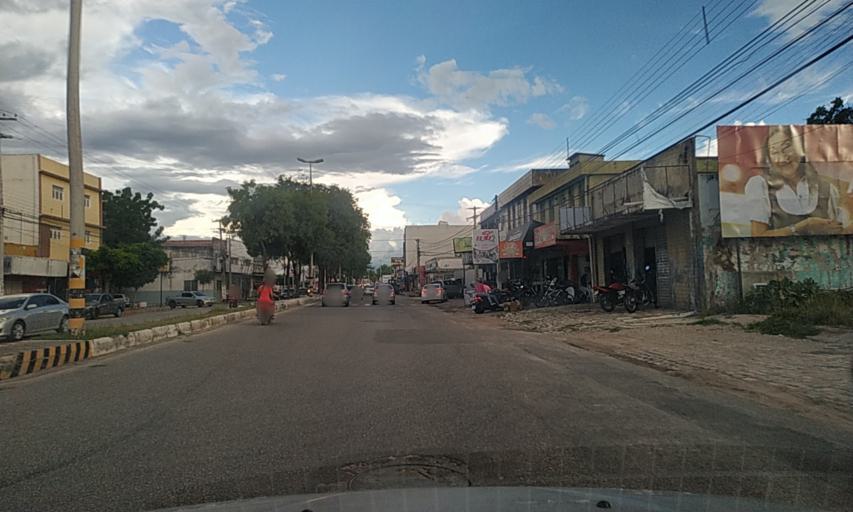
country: BR
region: Rio Grande do Norte
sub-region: Mossoro
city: Mossoro
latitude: -5.2014
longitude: -37.3386
